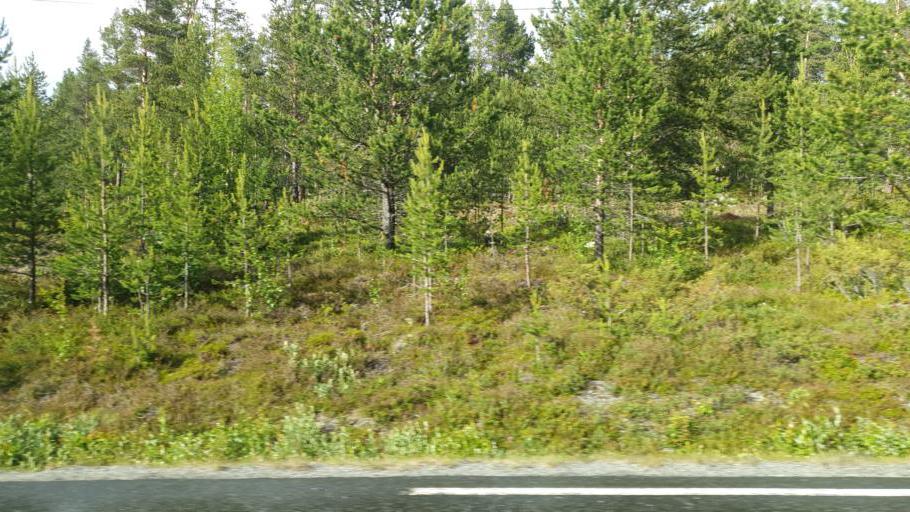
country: NO
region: Oppland
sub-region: Vaga
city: Vagamo
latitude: 61.8172
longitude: 8.9841
